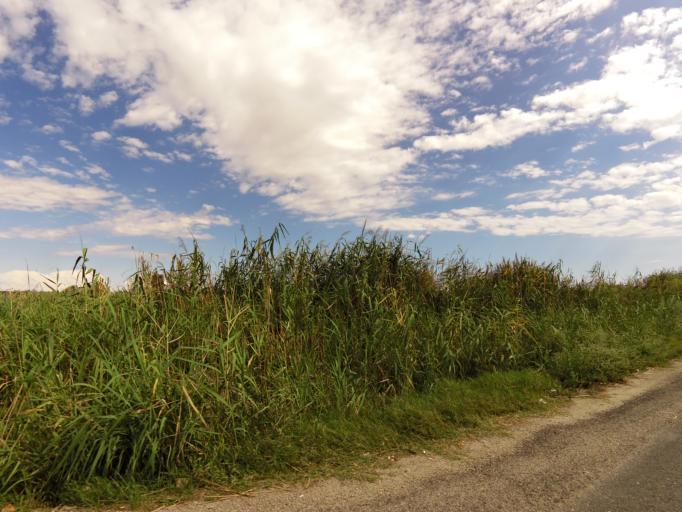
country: FR
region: Languedoc-Roussillon
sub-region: Departement du Gard
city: Le Grau-du-Roi
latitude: 43.5096
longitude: 4.1458
